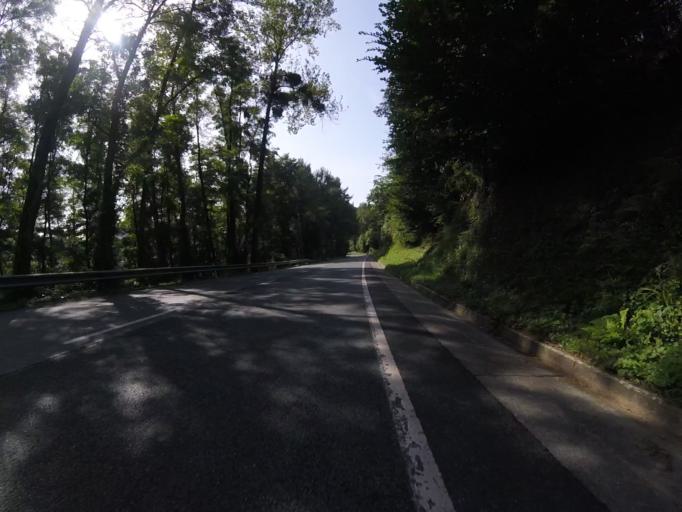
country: ES
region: Navarre
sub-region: Provincia de Navarra
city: Zugarramurdi
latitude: 43.2018
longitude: -1.4851
